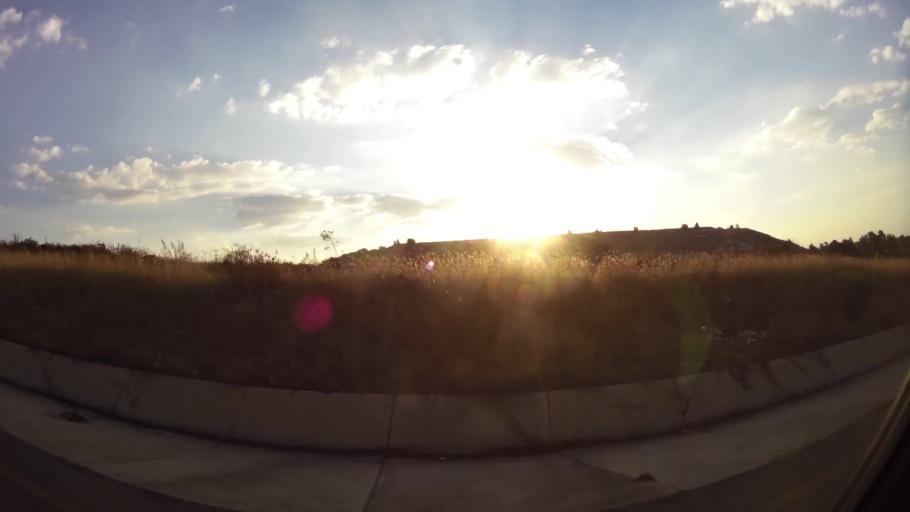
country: ZA
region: Gauteng
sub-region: City of Johannesburg Metropolitan Municipality
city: Roodepoort
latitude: -26.2083
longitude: 27.9038
